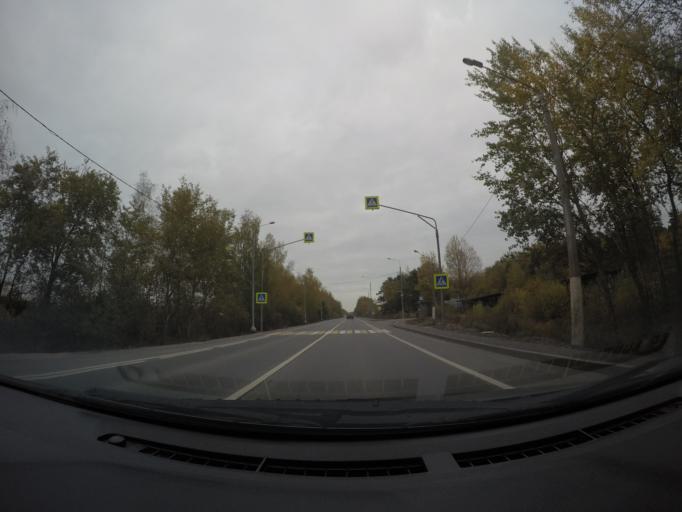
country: RU
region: Moskovskaya
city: Imeni Vorovskogo
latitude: 55.7222
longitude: 38.3699
